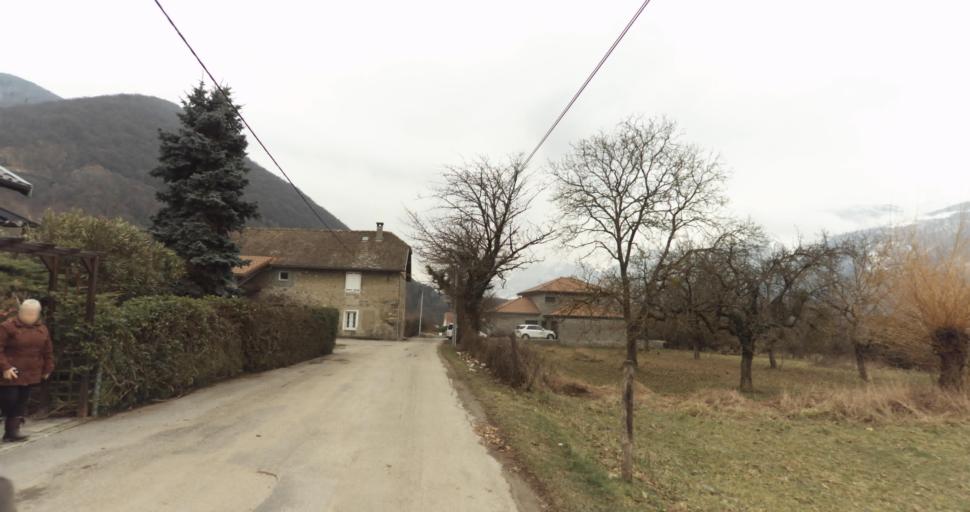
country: FR
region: Rhone-Alpes
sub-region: Departement de l'Isere
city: Vif
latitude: 45.0418
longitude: 5.6738
